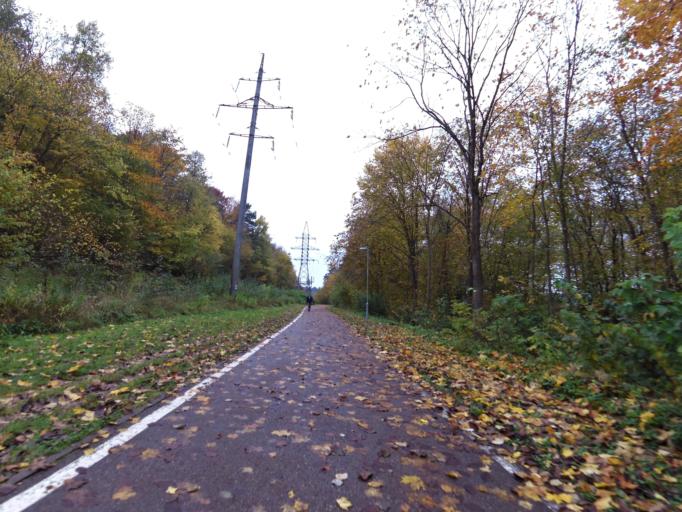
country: LT
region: Vilnius County
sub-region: Vilnius
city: Vilnius
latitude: 54.7295
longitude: 25.3009
